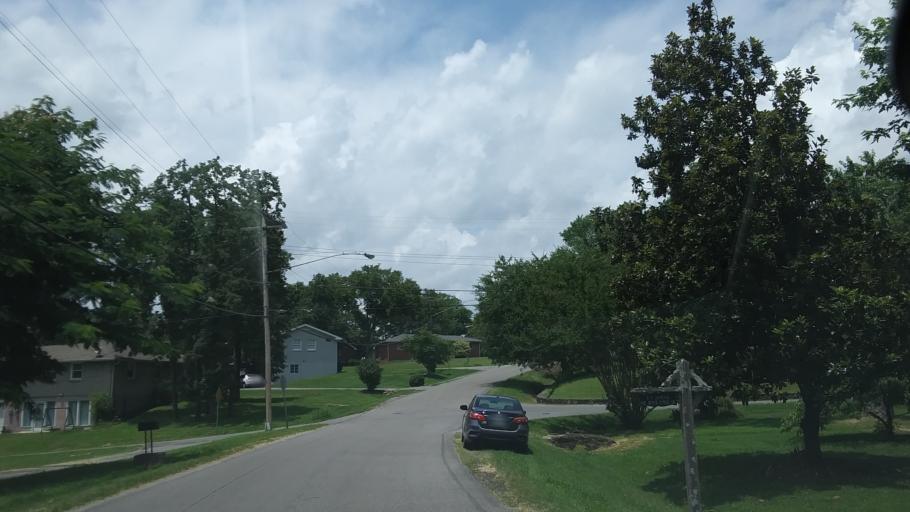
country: US
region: Tennessee
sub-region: Davidson County
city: Belle Meade
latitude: 36.1505
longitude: -86.8863
